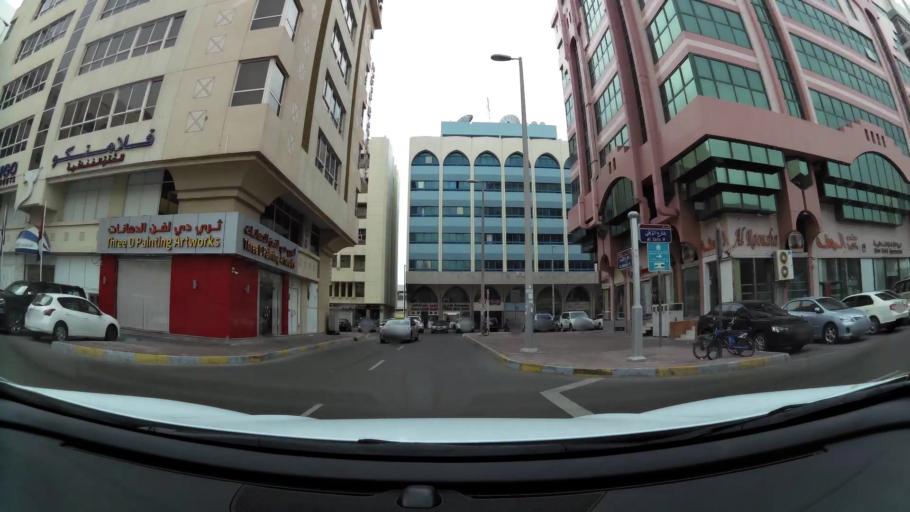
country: AE
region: Abu Dhabi
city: Abu Dhabi
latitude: 24.4800
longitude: 54.3663
